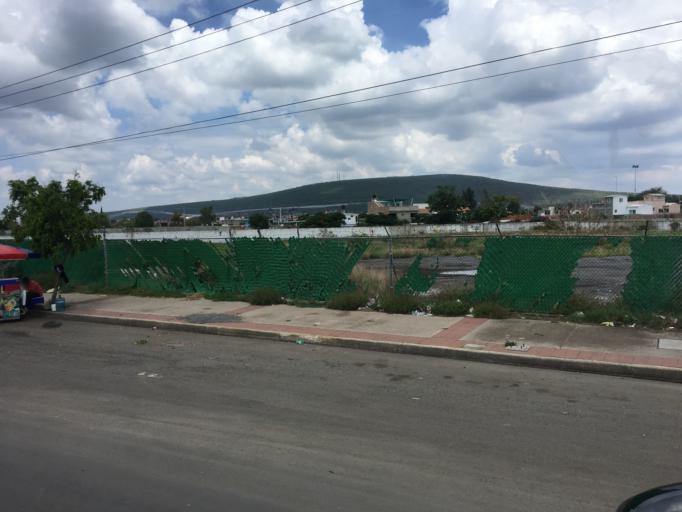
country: MX
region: Guanajuato
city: Irapuato
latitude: 20.7088
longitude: -101.3526
